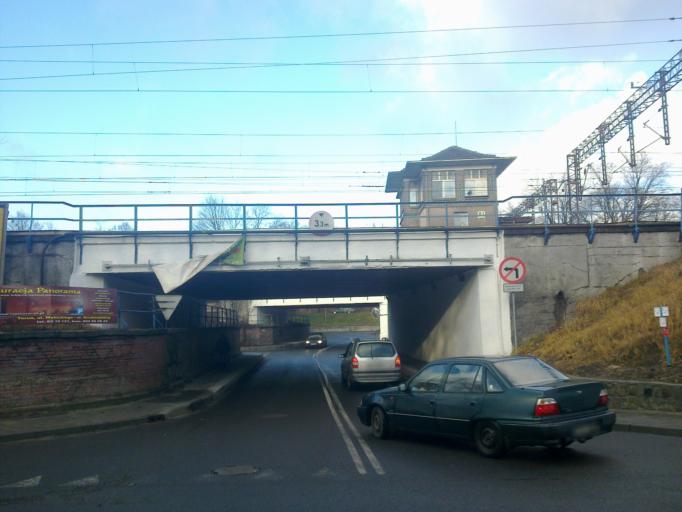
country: PL
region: Kujawsko-Pomorskie
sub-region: Torun
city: Torun
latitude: 53.0008
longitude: 18.6193
